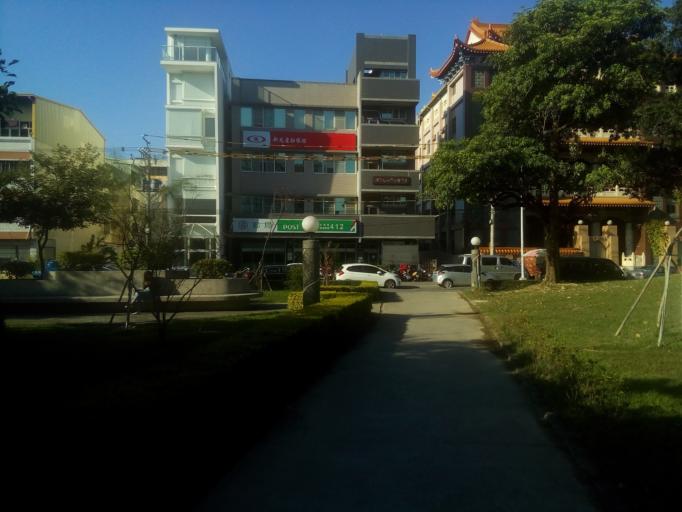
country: TW
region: Taiwan
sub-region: Taichung City
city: Taichung
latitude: 24.1049
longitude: 120.6788
